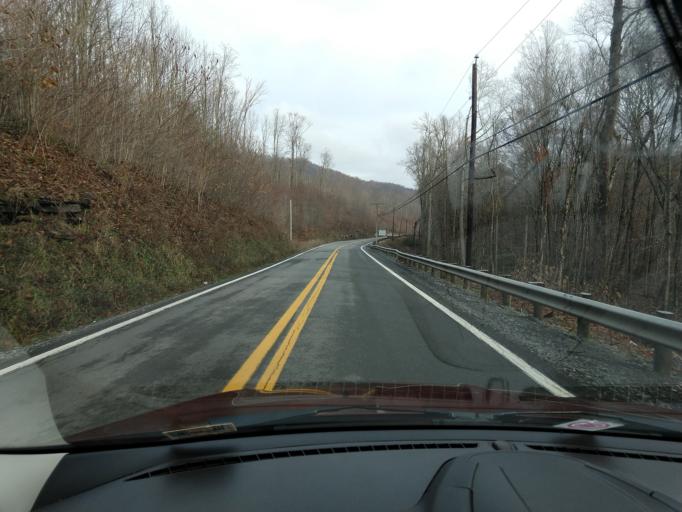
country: US
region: West Virginia
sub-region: Greenbrier County
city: Rainelle
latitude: 38.0838
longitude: -80.7083
